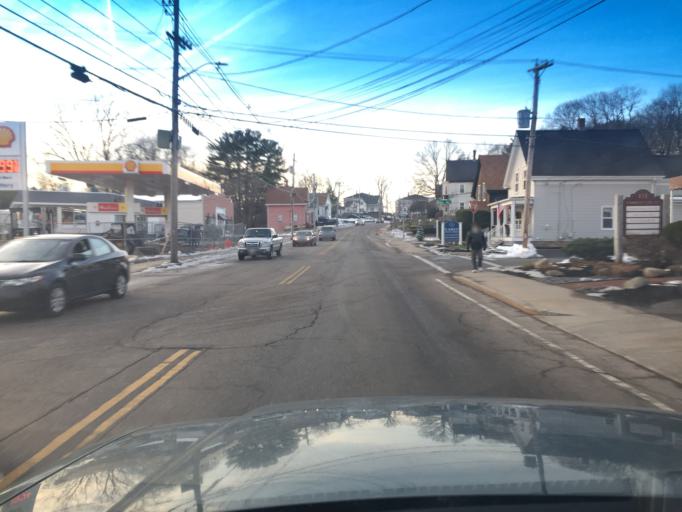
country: US
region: Massachusetts
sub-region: Norfolk County
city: Franklin
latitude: 42.0809
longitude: -71.3906
